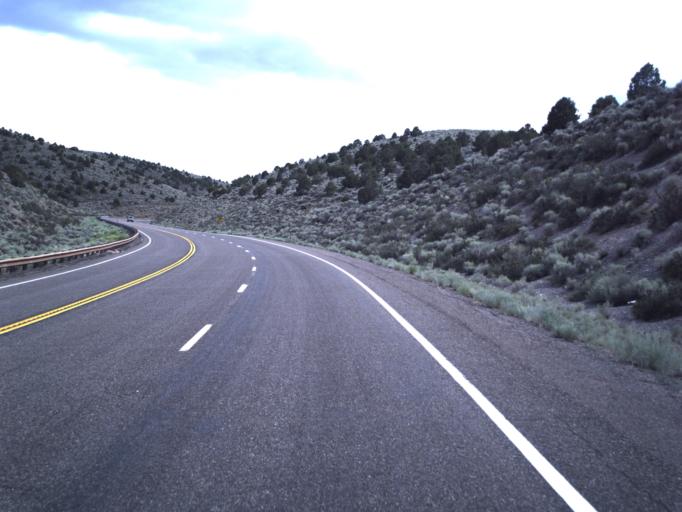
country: US
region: Utah
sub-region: Wayne County
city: Loa
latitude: 38.5210
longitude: -111.8333
